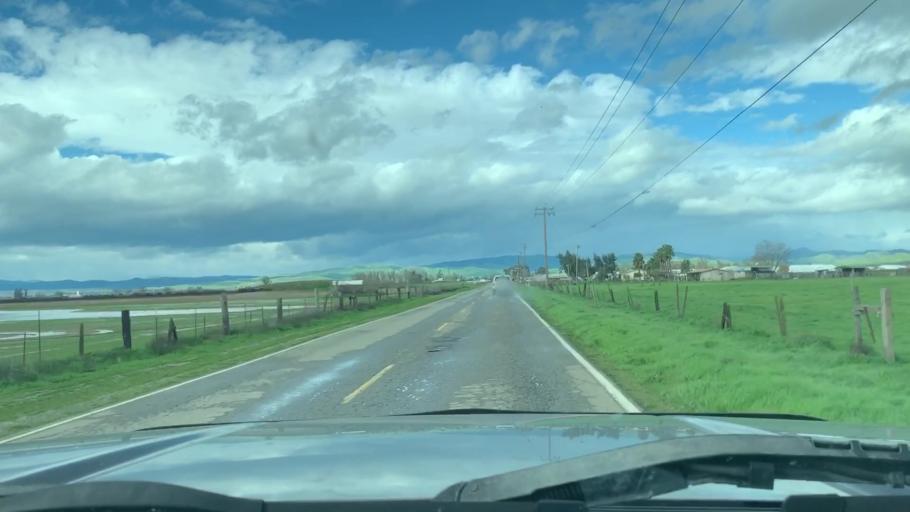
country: US
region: California
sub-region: Merced County
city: Los Banos
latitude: 37.1220
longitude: -120.9589
